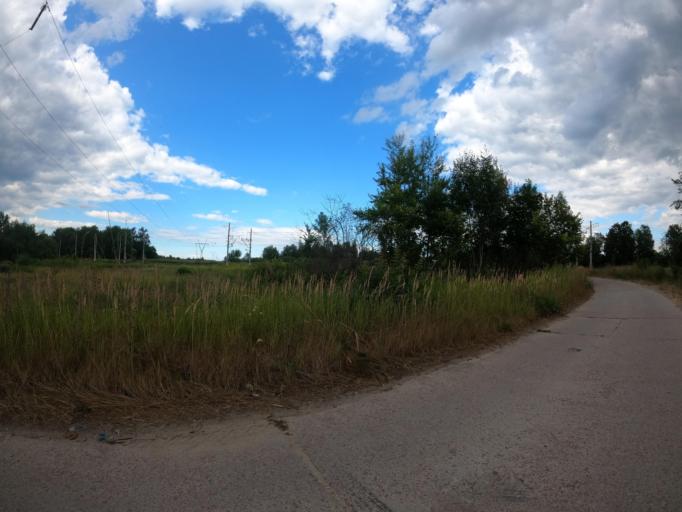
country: RU
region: Moskovskaya
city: Konobeyevo
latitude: 55.3938
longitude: 38.6703
